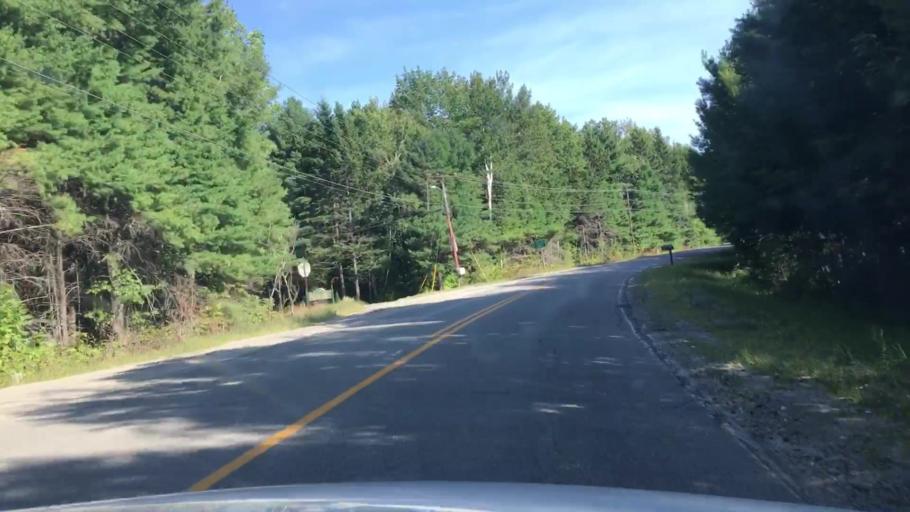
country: US
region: Maine
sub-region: Penobscot County
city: Enfield
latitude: 45.2368
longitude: -68.5459
